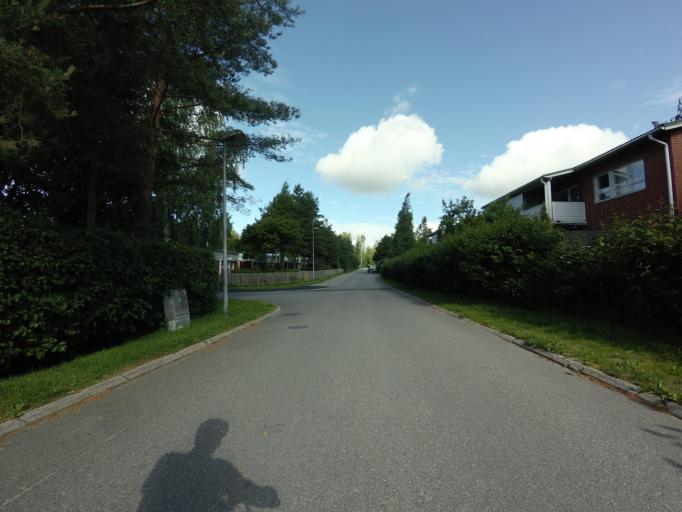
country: FI
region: Uusimaa
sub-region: Helsinki
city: Espoo
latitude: 60.1791
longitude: 24.6712
